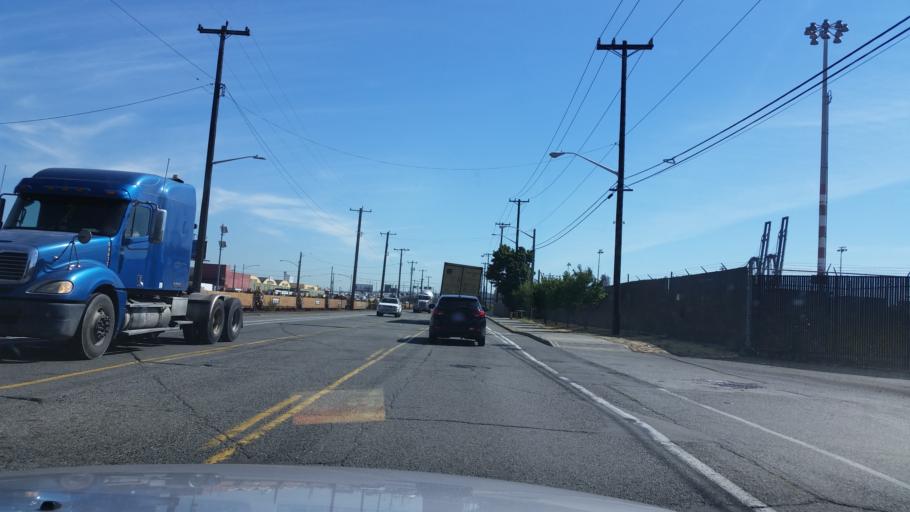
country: US
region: Washington
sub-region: King County
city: Seattle
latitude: 47.5800
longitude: -122.3401
